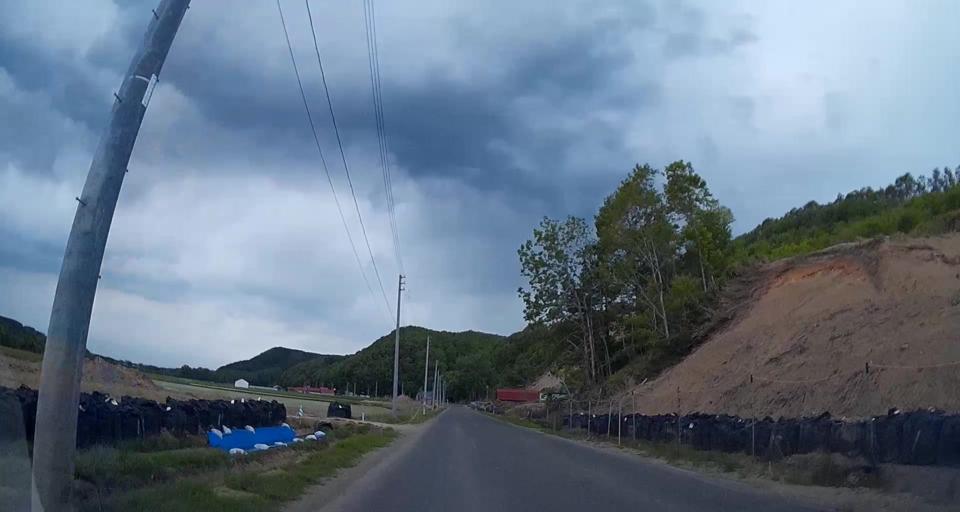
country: JP
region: Hokkaido
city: Chitose
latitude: 42.7584
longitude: 141.9653
